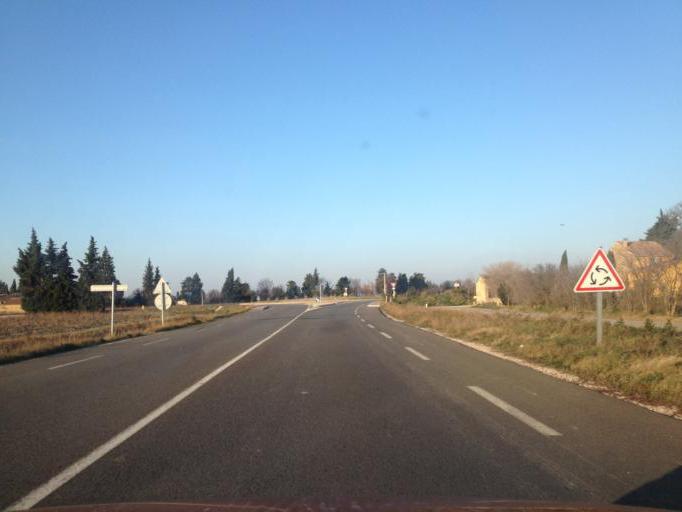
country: FR
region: Provence-Alpes-Cote d'Azur
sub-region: Departement du Vaucluse
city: Camaret-sur-Aigues
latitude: 44.1619
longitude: 4.8872
